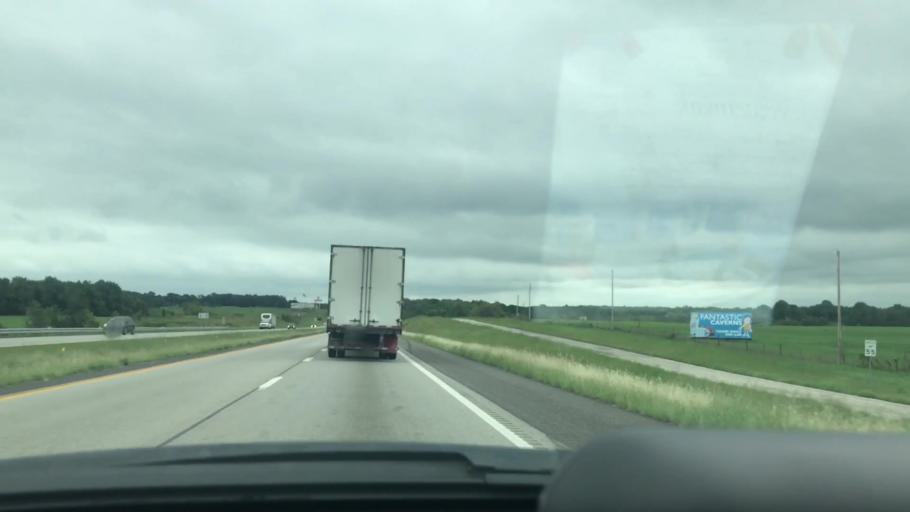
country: US
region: Missouri
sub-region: Christian County
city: Billings
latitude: 37.1859
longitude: -93.5857
